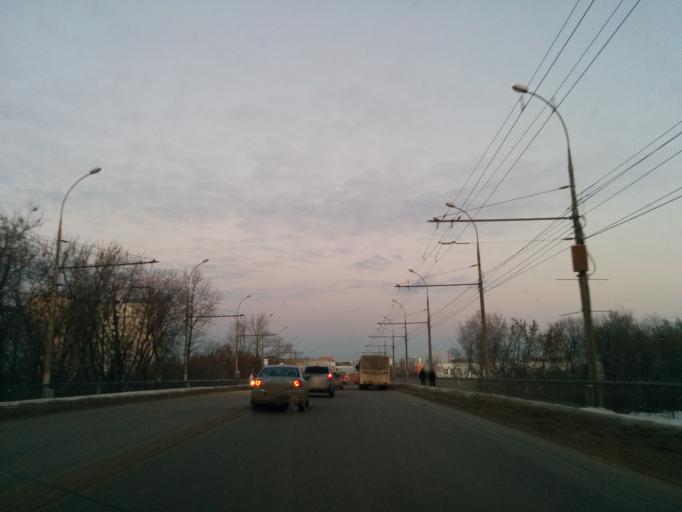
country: RU
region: Perm
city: Perm
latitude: 57.9926
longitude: 56.2036
